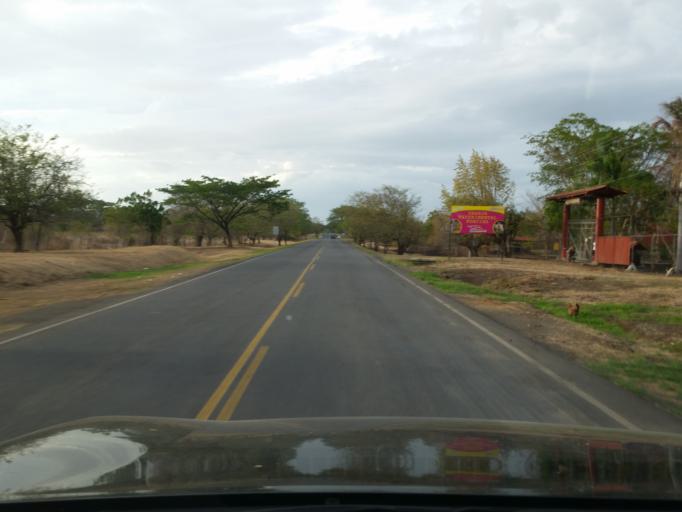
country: NI
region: Rivas
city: Belen
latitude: 11.5697
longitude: -85.8988
